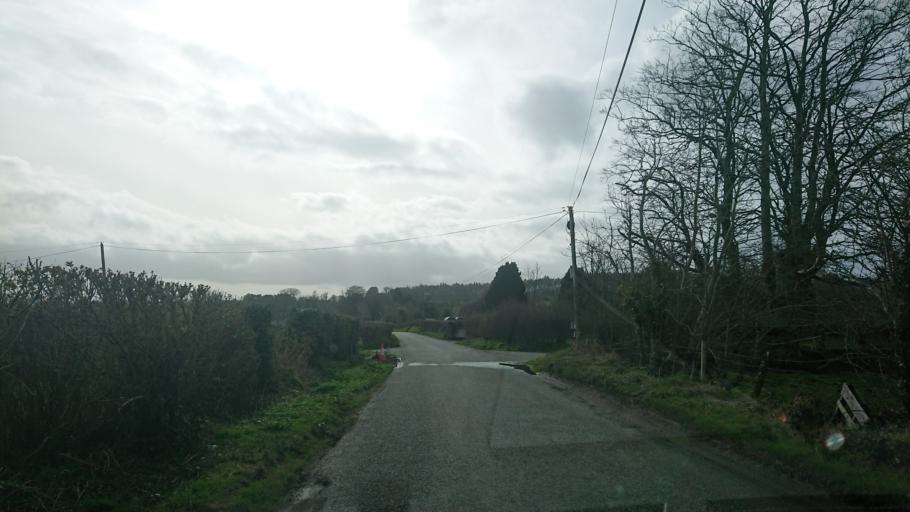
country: IE
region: Leinster
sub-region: Wicklow
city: Blessington
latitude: 53.1595
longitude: -6.5576
